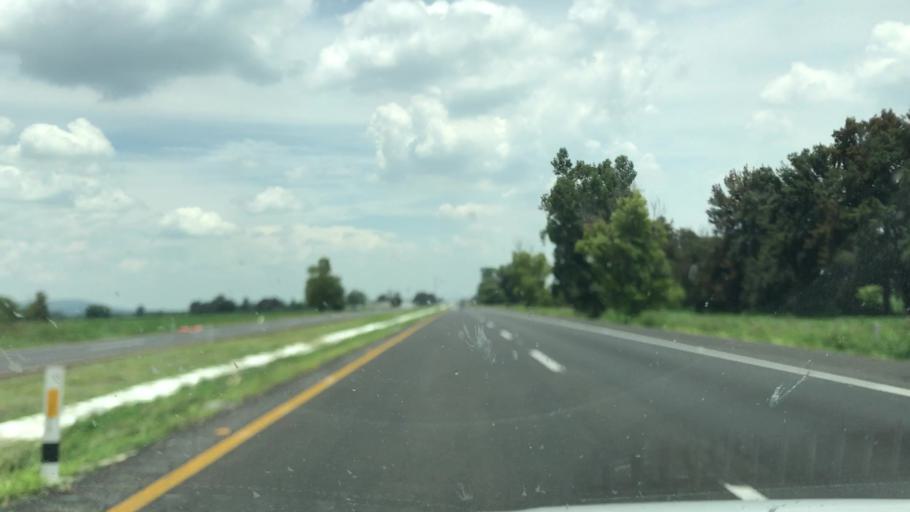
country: MX
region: Guanajuato
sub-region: Salamanca
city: San Vicente de Flores
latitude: 20.6280
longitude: -101.2461
